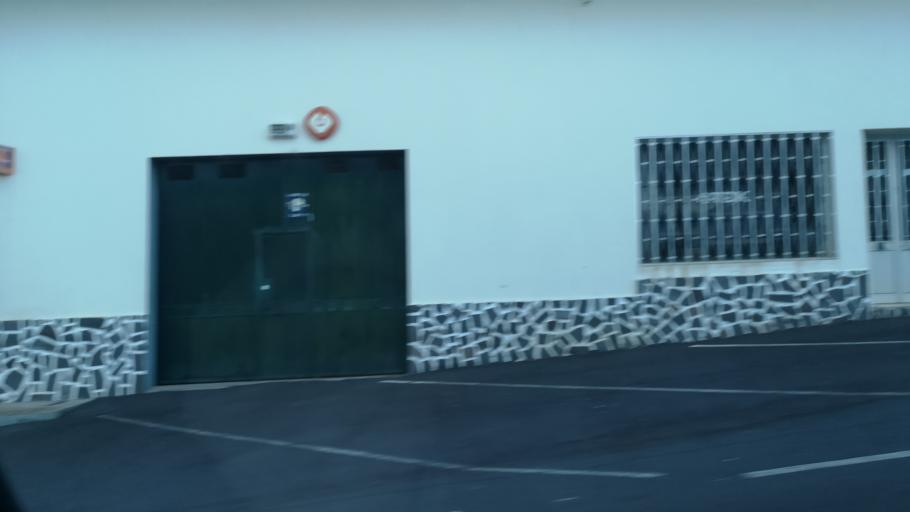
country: PT
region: Madeira
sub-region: Santa Cruz
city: Santa Cruz
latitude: 32.6740
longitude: -16.8181
